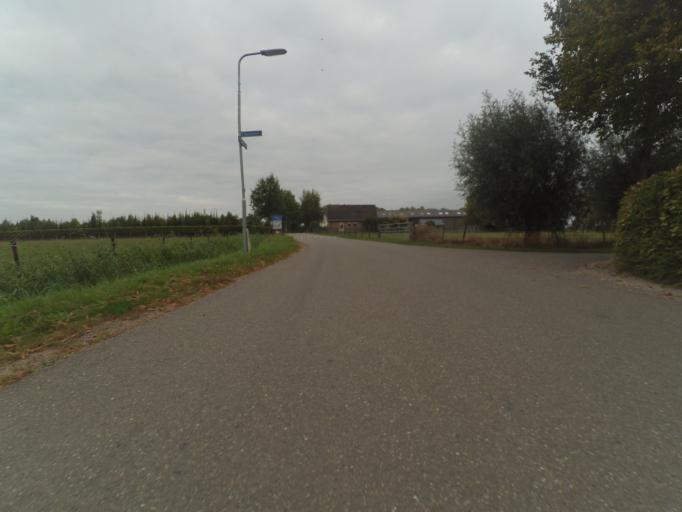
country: NL
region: Gelderland
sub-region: Gemeente Geldermalsen
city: Geldermalsen
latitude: 51.9307
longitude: 5.3082
